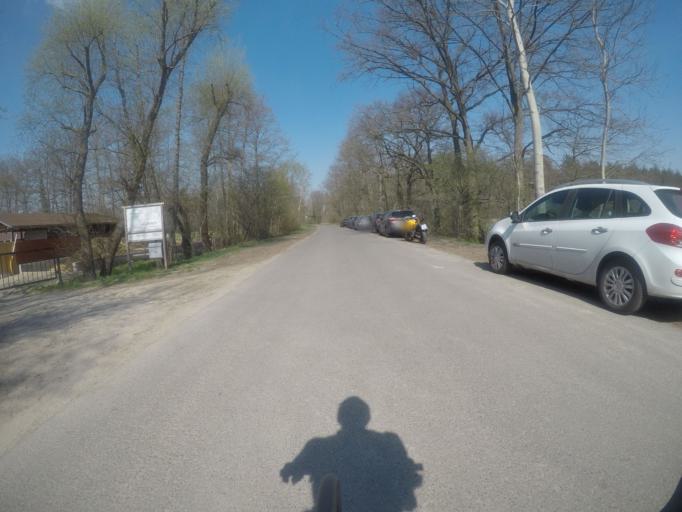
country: DE
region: Brandenburg
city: Falkensee
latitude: 52.6280
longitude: 13.1277
